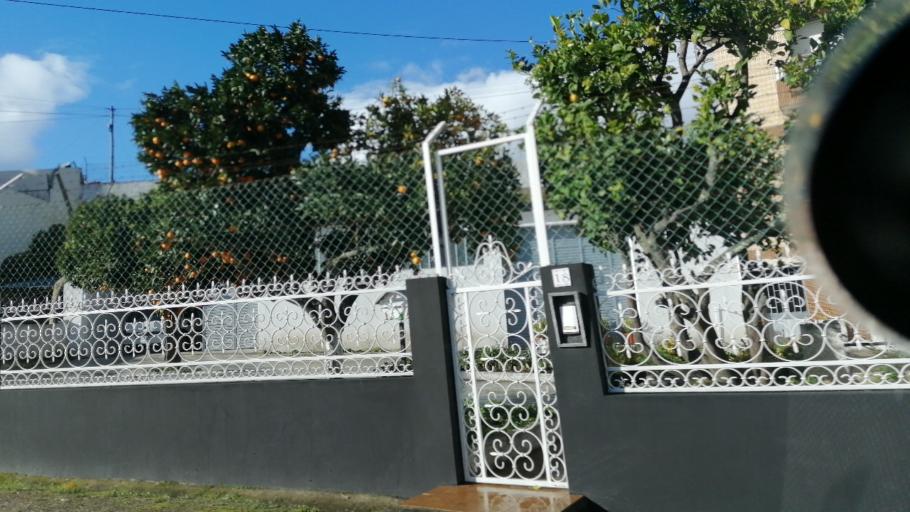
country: PT
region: Viseu
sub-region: Lamego
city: Lamego
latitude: 41.1251
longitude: -7.7901
